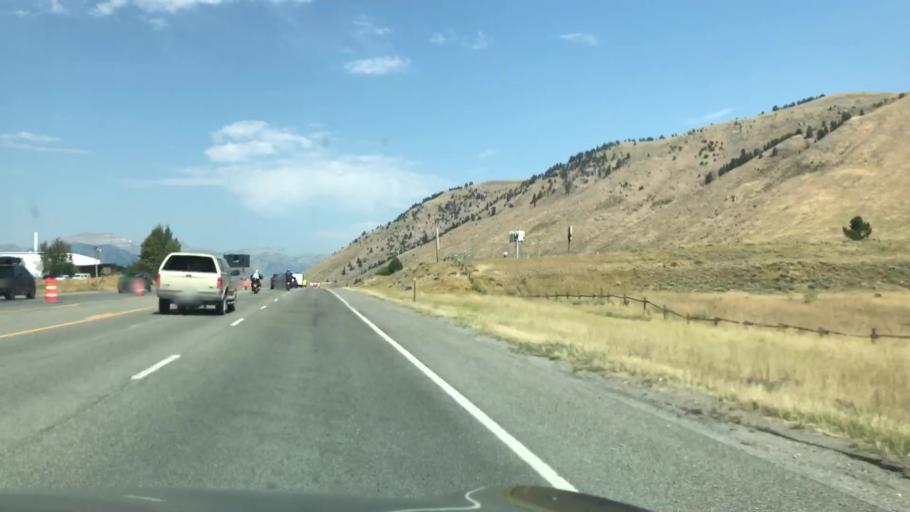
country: US
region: Wyoming
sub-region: Teton County
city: South Park
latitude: 43.4169
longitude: -110.7740
